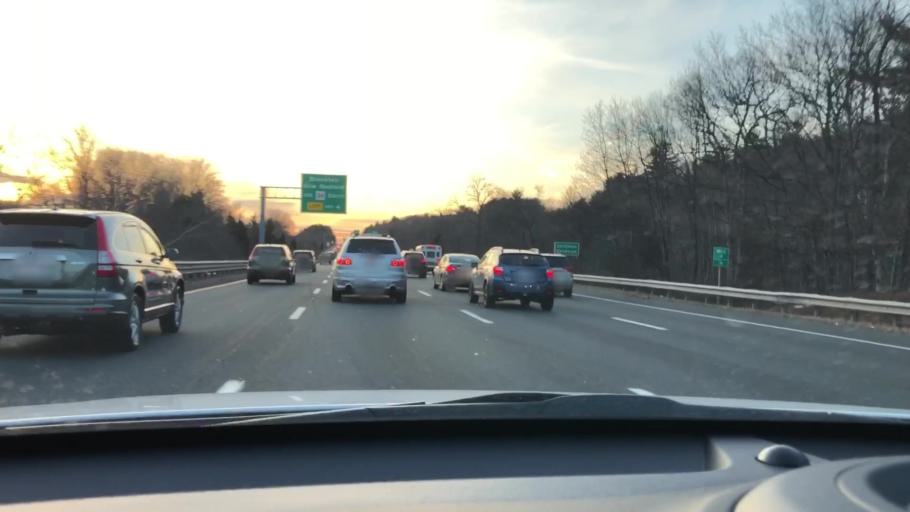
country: US
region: Massachusetts
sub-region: Norfolk County
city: Milton
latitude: 42.2057
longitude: -71.0584
